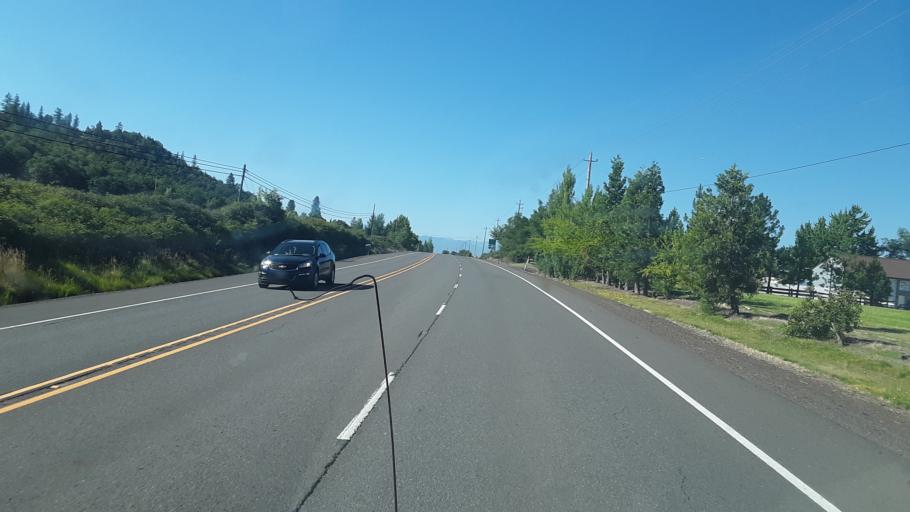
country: US
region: Oregon
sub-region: Jackson County
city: Eagle Point
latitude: 42.5336
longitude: -122.8142
